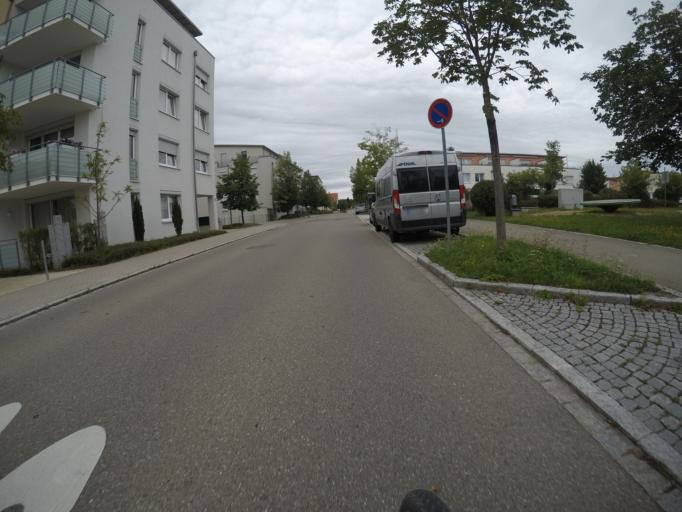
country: DE
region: Baden-Wuerttemberg
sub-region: Regierungsbezirk Stuttgart
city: Holzgerlingen
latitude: 48.6441
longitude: 9.0061
